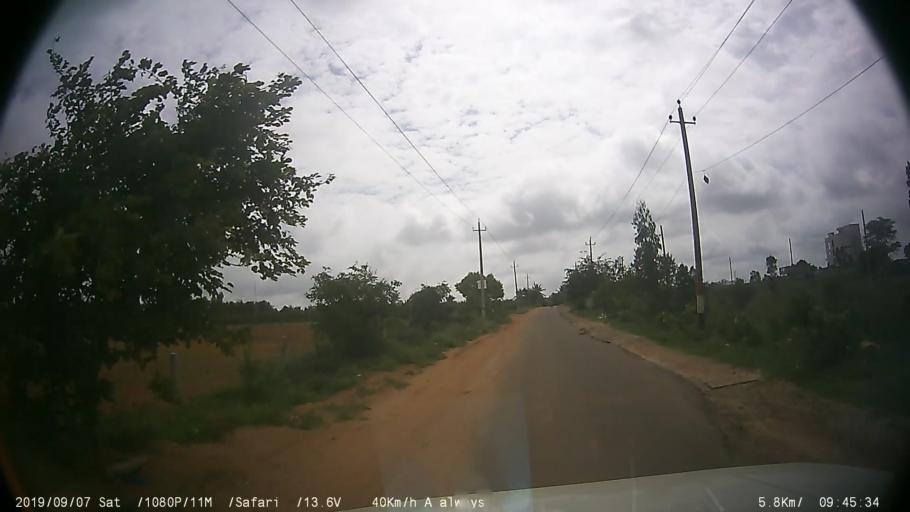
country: IN
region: Karnataka
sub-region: Bangalore Urban
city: Anekal
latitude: 12.8145
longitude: 77.6479
